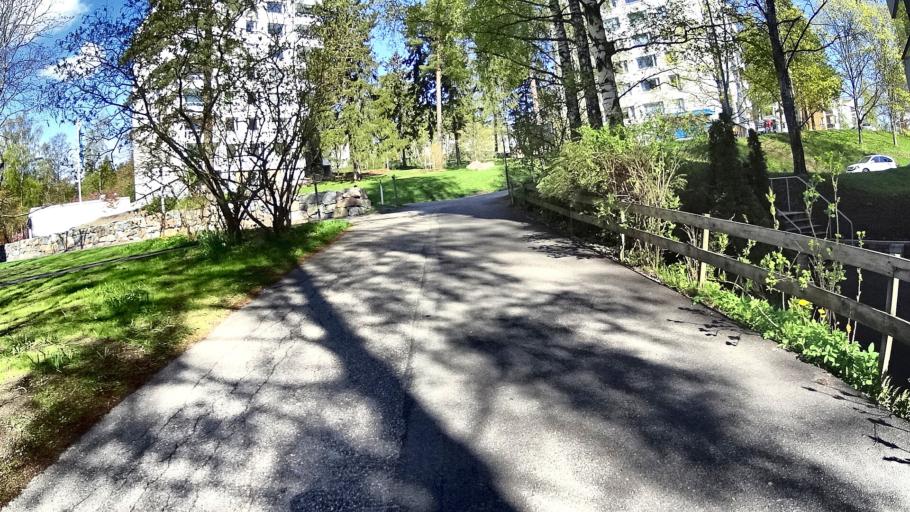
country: FI
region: Uusimaa
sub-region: Helsinki
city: Vantaa
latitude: 60.1987
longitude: 25.0601
